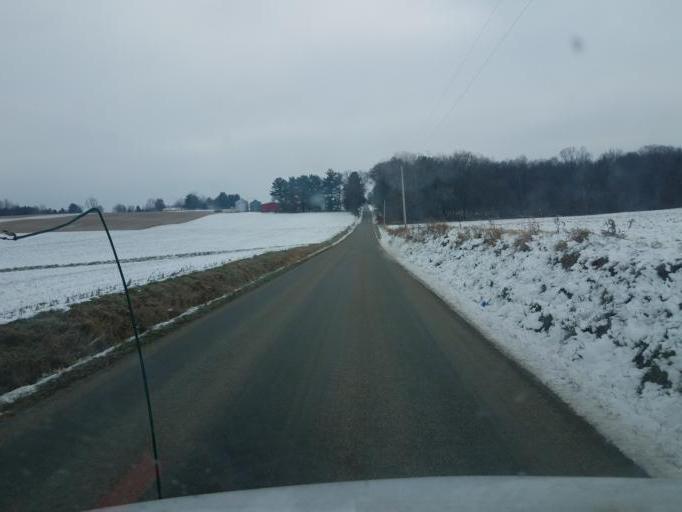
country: US
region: Ohio
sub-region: Knox County
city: Fredericktown
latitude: 40.5297
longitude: -82.5708
